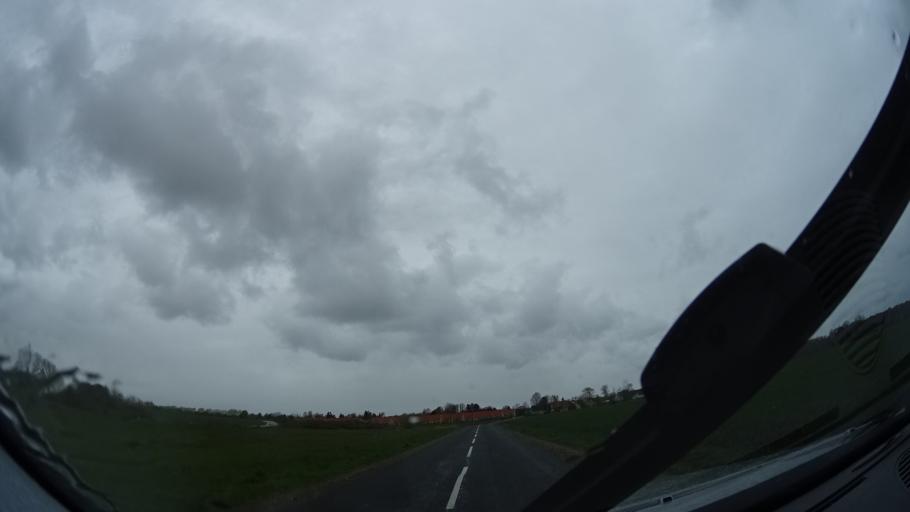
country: DK
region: Zealand
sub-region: Holbaek Kommune
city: Vipperod
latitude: 55.7013
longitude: 11.7793
